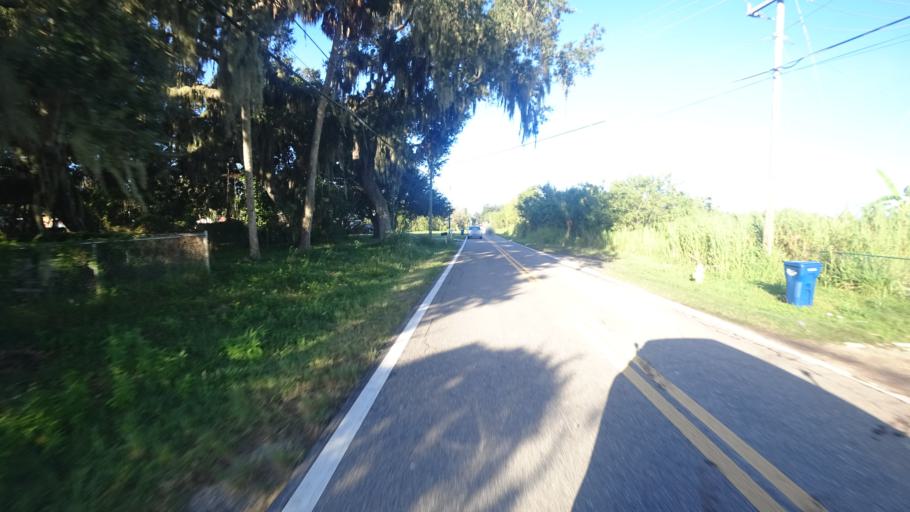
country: US
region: Florida
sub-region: Manatee County
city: Memphis
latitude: 27.5579
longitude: -82.5502
